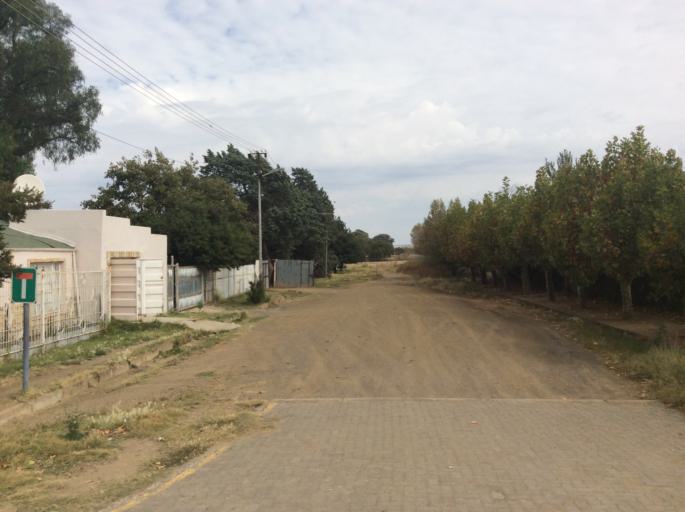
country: LS
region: Mafeteng
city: Mafeteng
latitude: -29.7284
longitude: 27.0366
